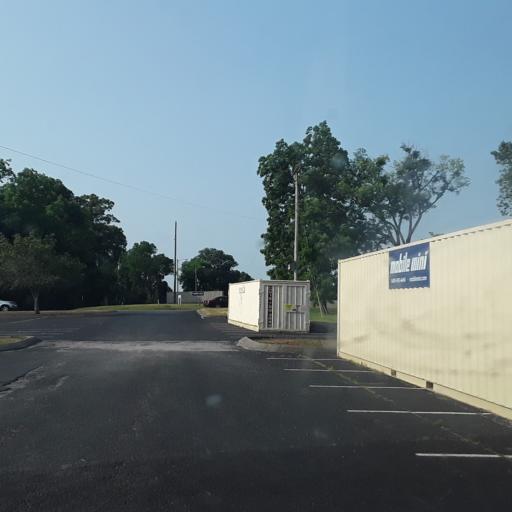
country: US
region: Tennessee
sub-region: Davidson County
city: Oak Hill
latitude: 36.0617
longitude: -86.7463
